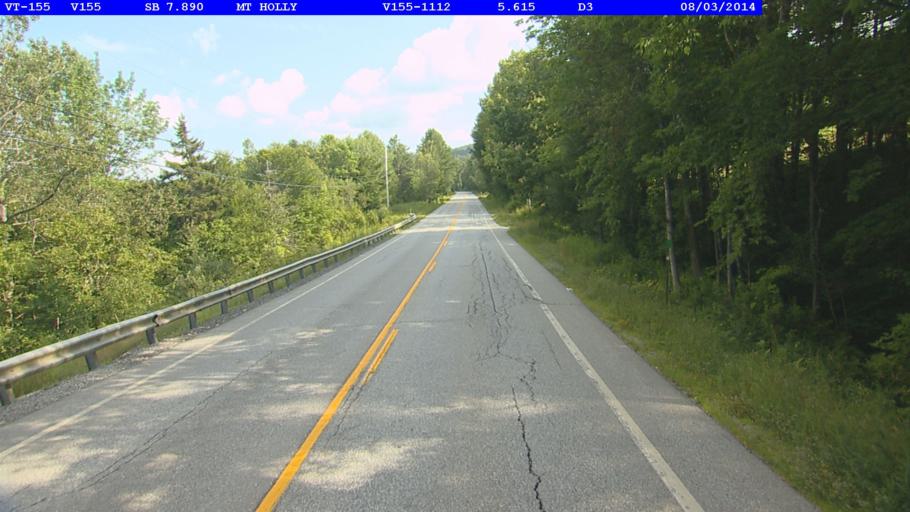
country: US
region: Vermont
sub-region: Rutland County
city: Rutland
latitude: 43.4238
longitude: -72.8563
